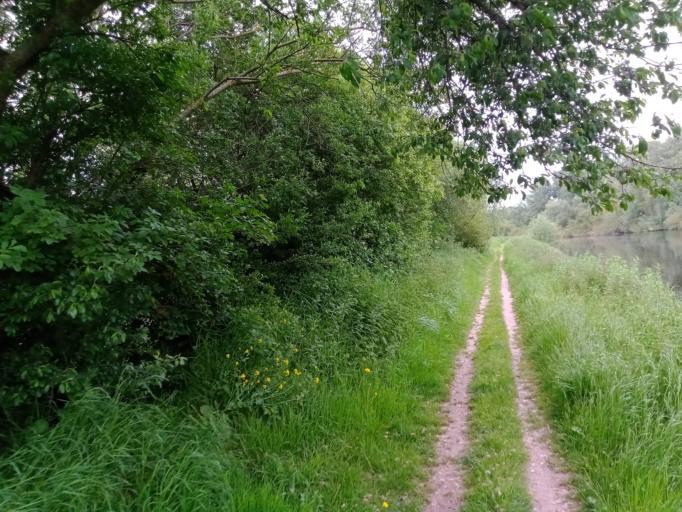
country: IE
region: Leinster
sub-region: County Carlow
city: Carlow
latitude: 52.8202
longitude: -6.9472
